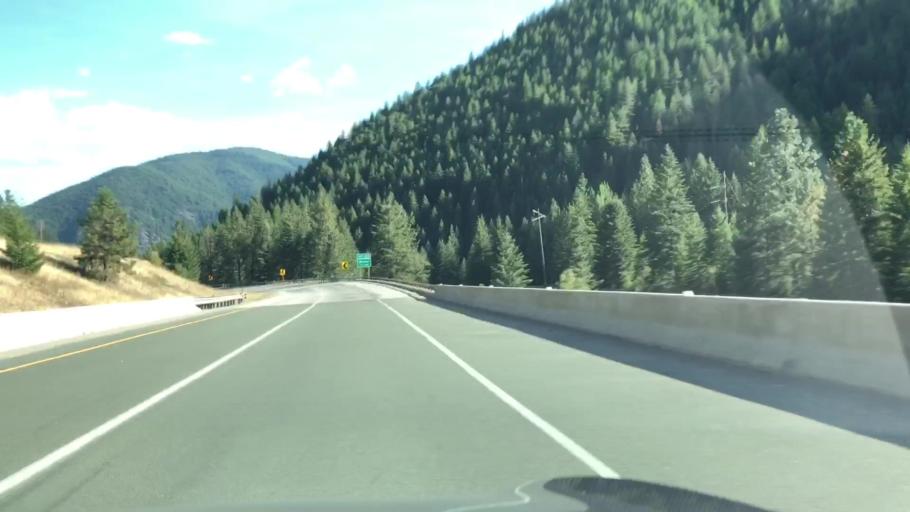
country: US
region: Montana
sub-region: Sanders County
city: Thompson Falls
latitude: 47.3294
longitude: -115.2582
